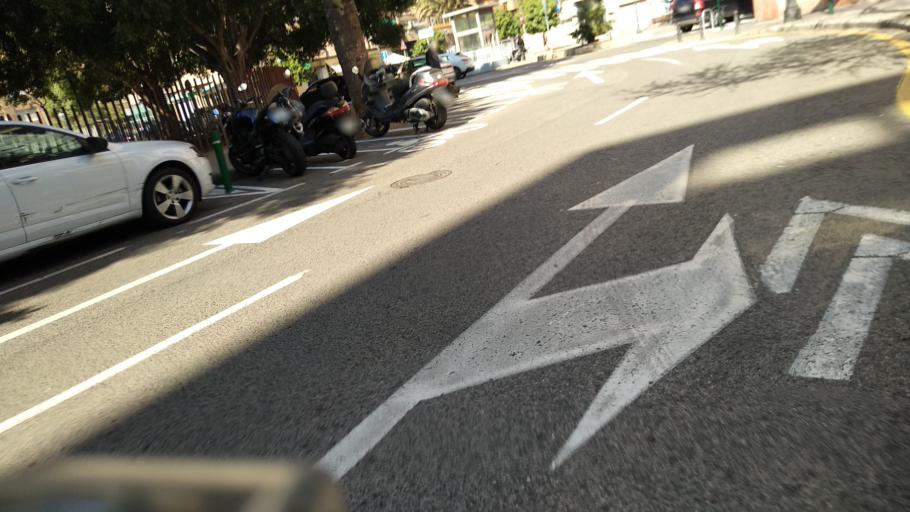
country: ES
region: Valencia
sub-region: Provincia de Valencia
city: Valencia
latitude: 39.4707
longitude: -0.3559
